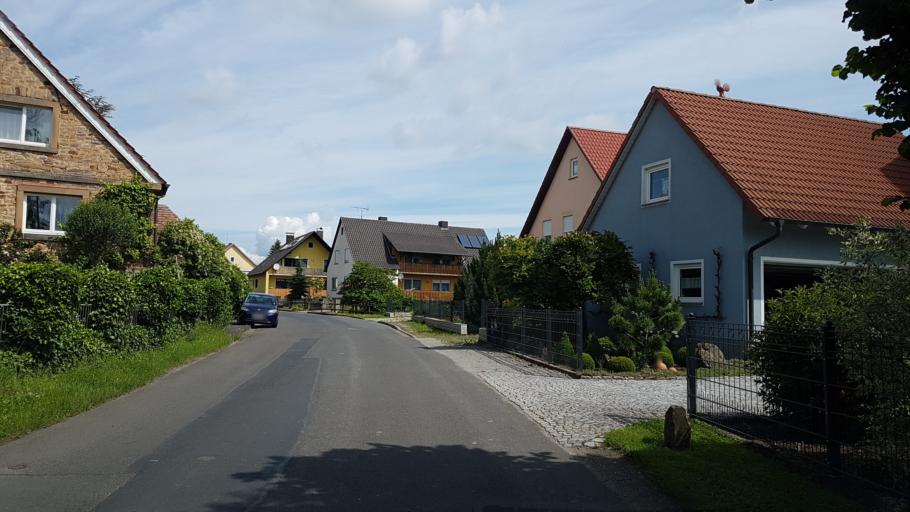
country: DE
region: Bavaria
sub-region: Regierungsbezirk Unterfranken
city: Lulsfeld
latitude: 49.8512
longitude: 10.3298
